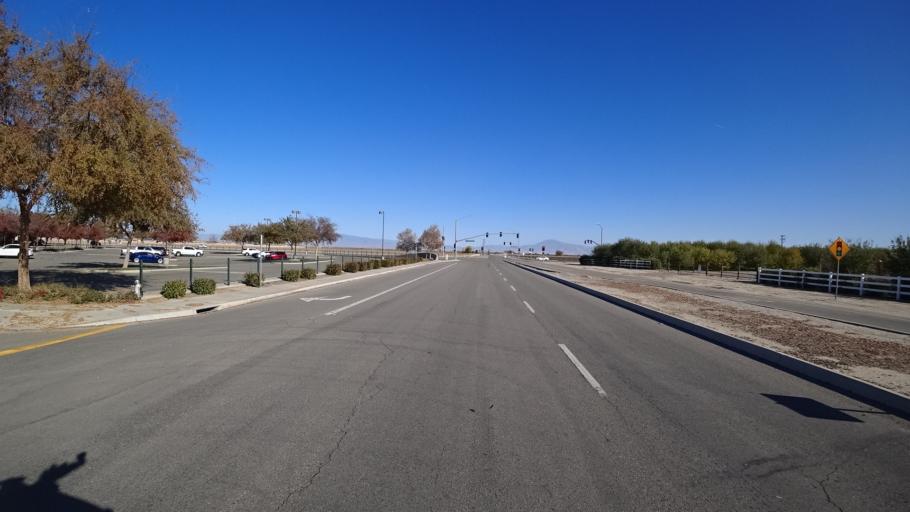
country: US
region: California
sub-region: Kern County
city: Greenacres
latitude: 35.2817
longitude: -119.1112
